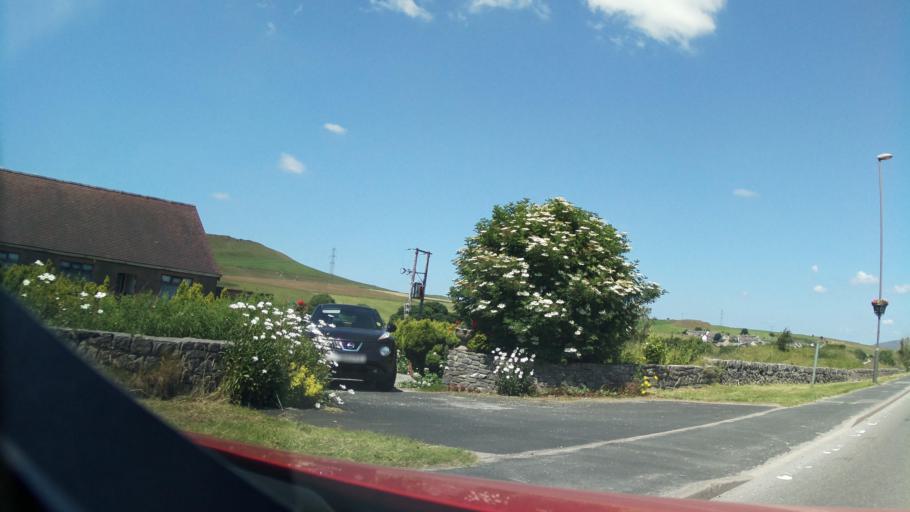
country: GB
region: England
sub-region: Derbyshire
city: Chapel en le Frith
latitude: 53.2946
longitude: -1.8881
